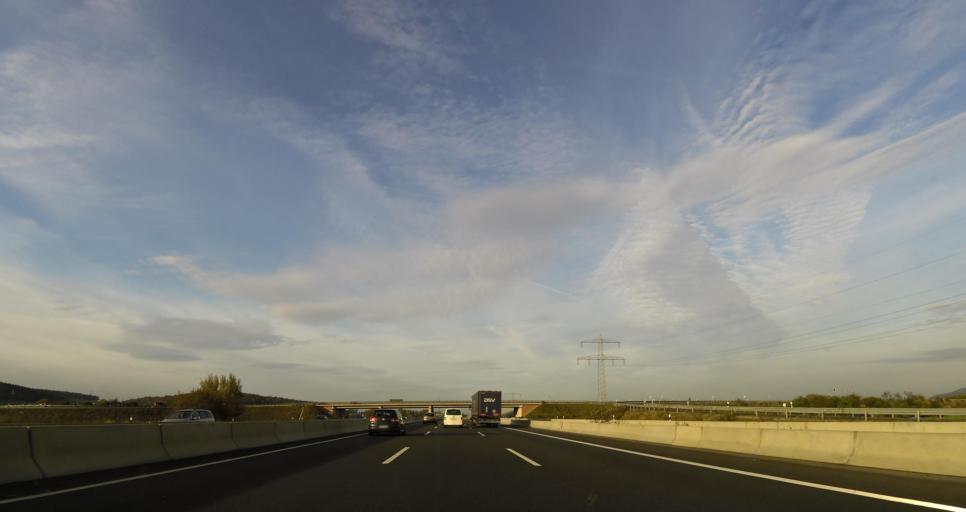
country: DE
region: Lower Saxony
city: Goettingen
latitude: 51.5549
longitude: 9.8793
